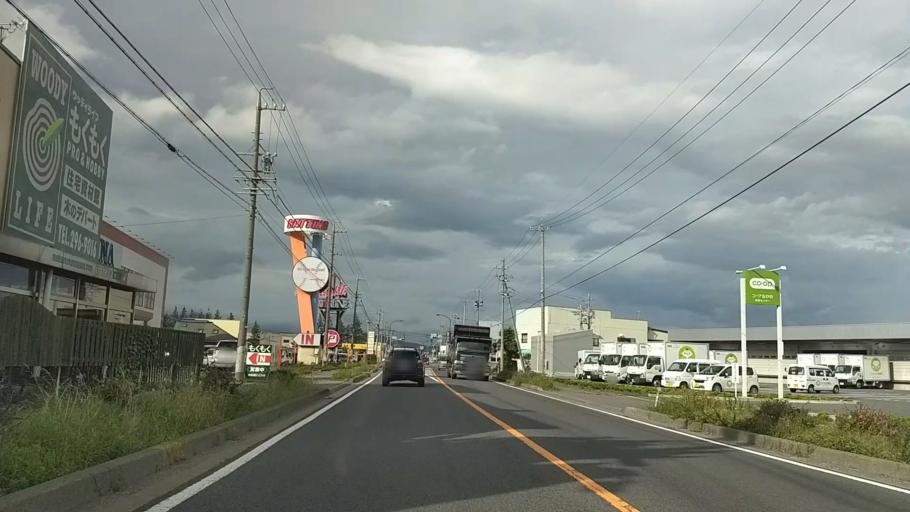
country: JP
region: Nagano
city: Suzaka
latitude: 36.6669
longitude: 138.2635
